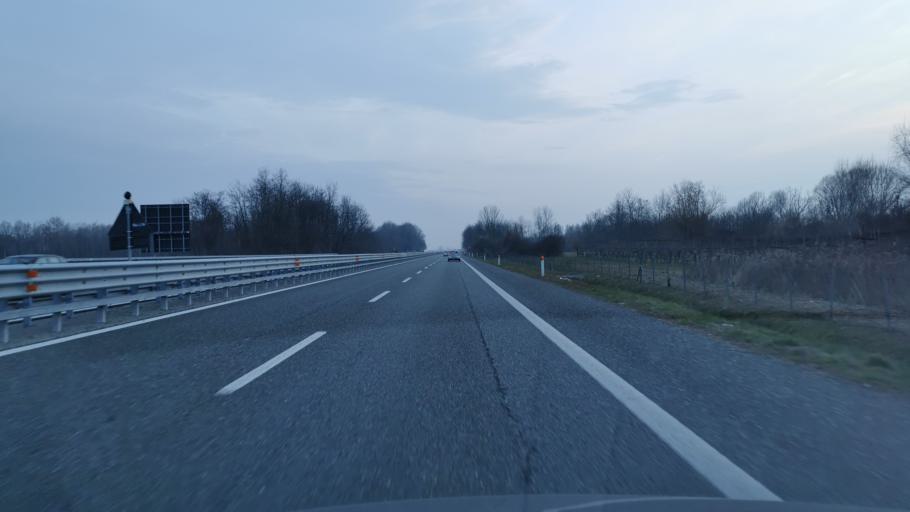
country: IT
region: Piedmont
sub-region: Provincia di Torino
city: San Giusto Canavese
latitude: 45.3112
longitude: 7.8188
